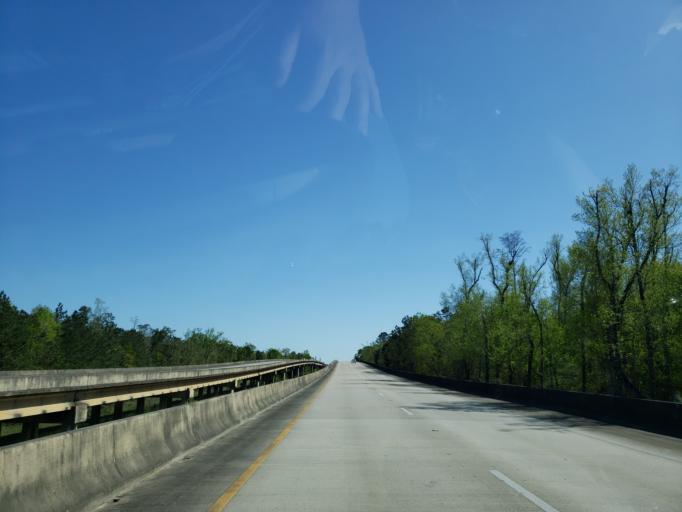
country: US
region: Mississippi
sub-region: Harrison County
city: Lyman
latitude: 30.4892
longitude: -89.0289
